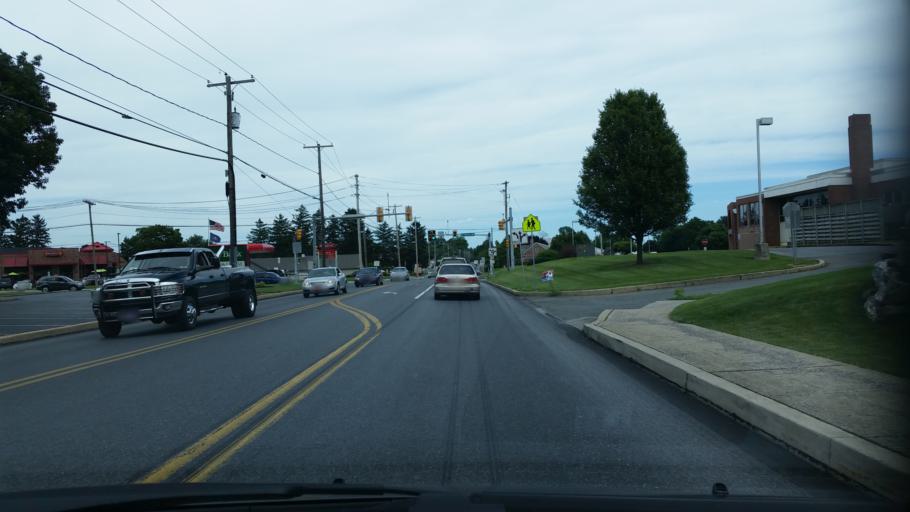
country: US
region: Pennsylvania
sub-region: Lancaster County
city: Lampeter
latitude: 40.0395
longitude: -76.2093
